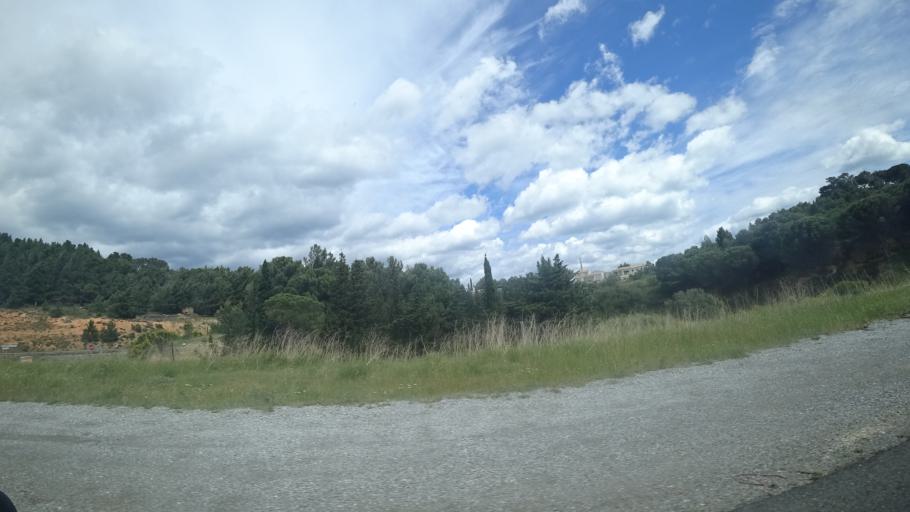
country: FR
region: Languedoc-Roussillon
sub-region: Departement de l'Aude
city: Leucate
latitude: 42.9121
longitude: 3.0209
